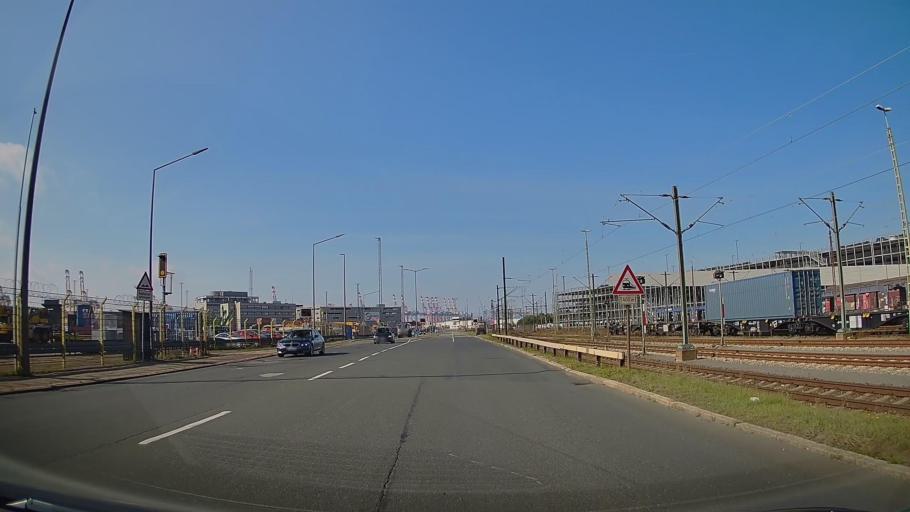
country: DE
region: Bremen
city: Bremerhaven
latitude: 53.5789
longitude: 8.5536
